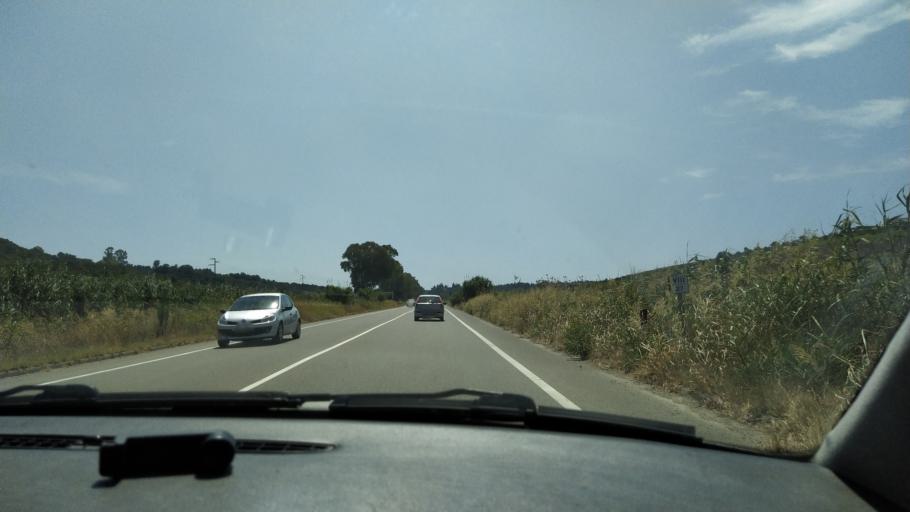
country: IT
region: Basilicate
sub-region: Provincia di Matera
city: Bernalda
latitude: 40.4415
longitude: 16.7827
